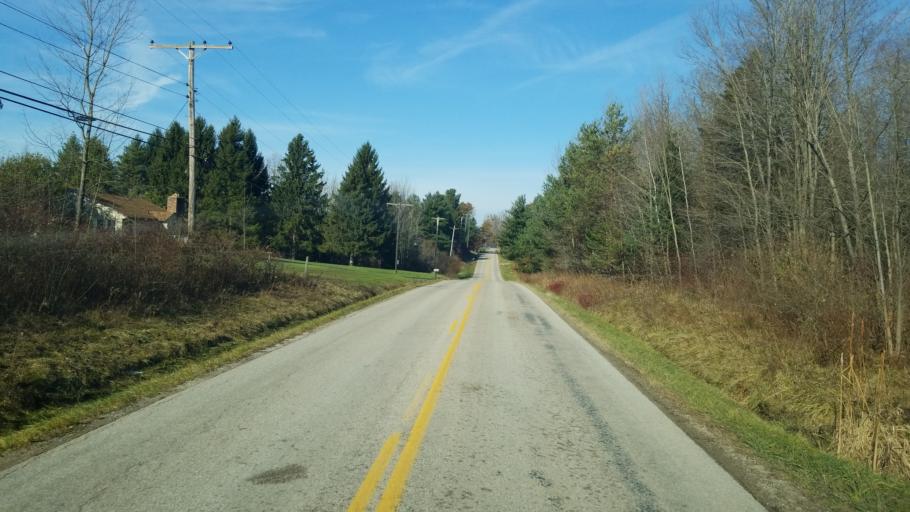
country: US
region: Ohio
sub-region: Ashtabula County
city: Jefferson
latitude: 41.7322
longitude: -80.7275
